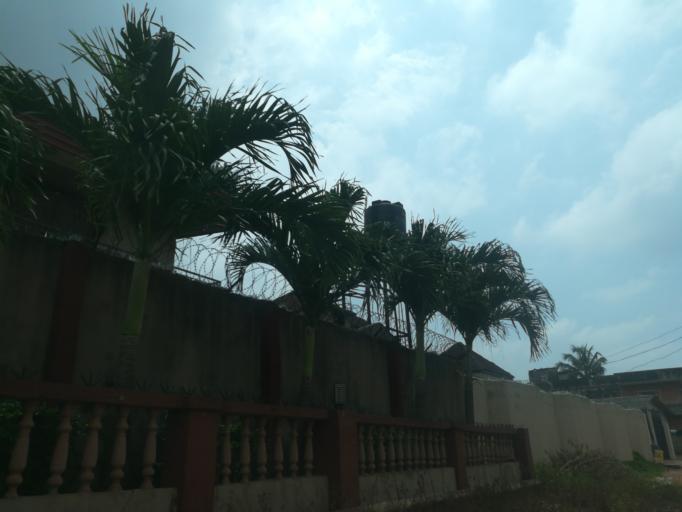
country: NG
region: Lagos
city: Ikorodu
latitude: 6.6186
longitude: 3.5192
